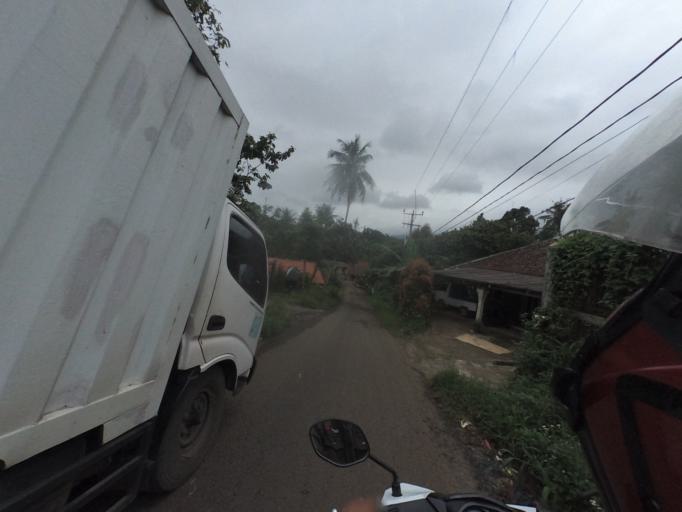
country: ID
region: West Java
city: Bogor
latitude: -6.6372
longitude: 106.7335
